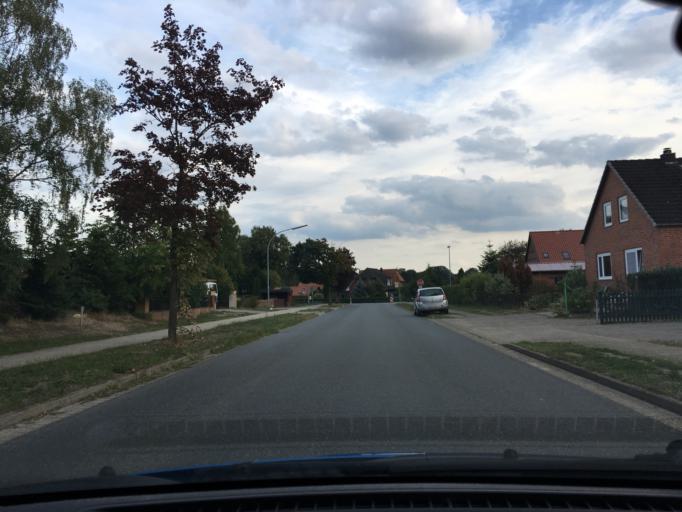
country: DE
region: Lower Saxony
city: Westergellersen
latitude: 53.2366
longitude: 10.2413
